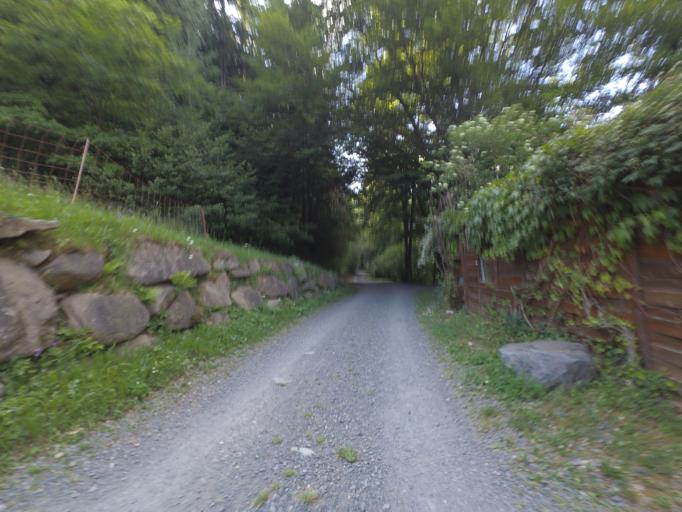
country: AT
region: Carinthia
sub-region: Politischer Bezirk Spittal an der Drau
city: Millstatt
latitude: 46.7763
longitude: 13.5979
